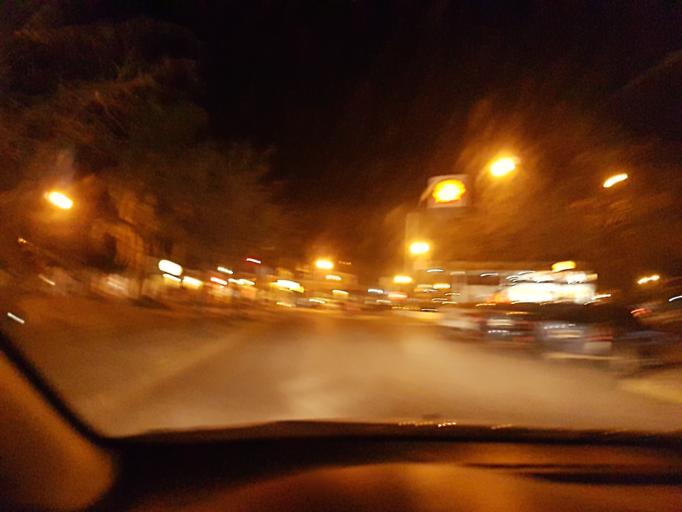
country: AR
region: Cordoba
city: Villa Allende
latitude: -31.2881
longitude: -64.2934
